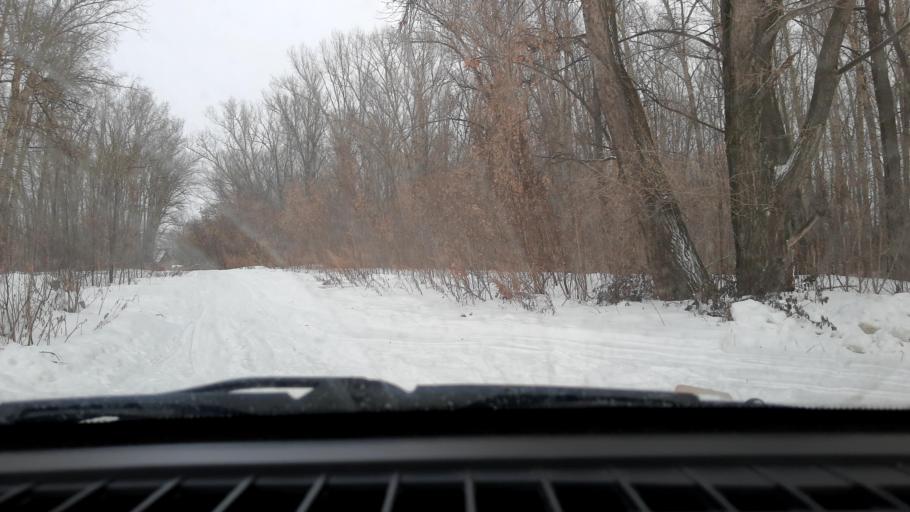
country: RU
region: Bashkortostan
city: Ufa
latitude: 54.7223
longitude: 55.9058
